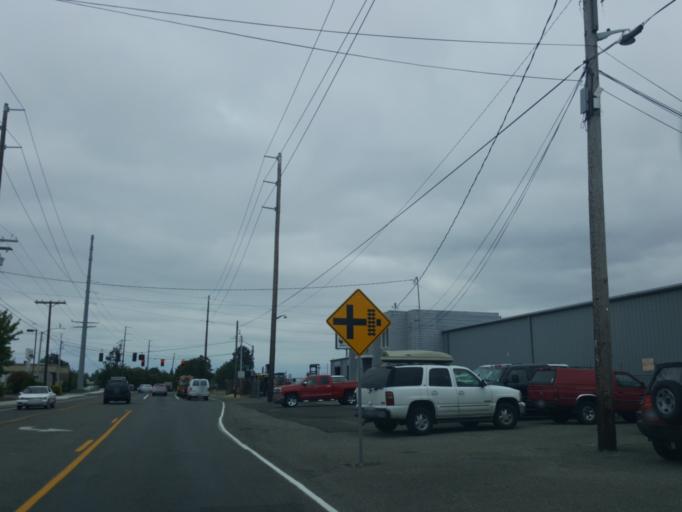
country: US
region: Washington
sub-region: Pierce County
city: Lakewood
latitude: 47.1653
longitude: -122.4943
